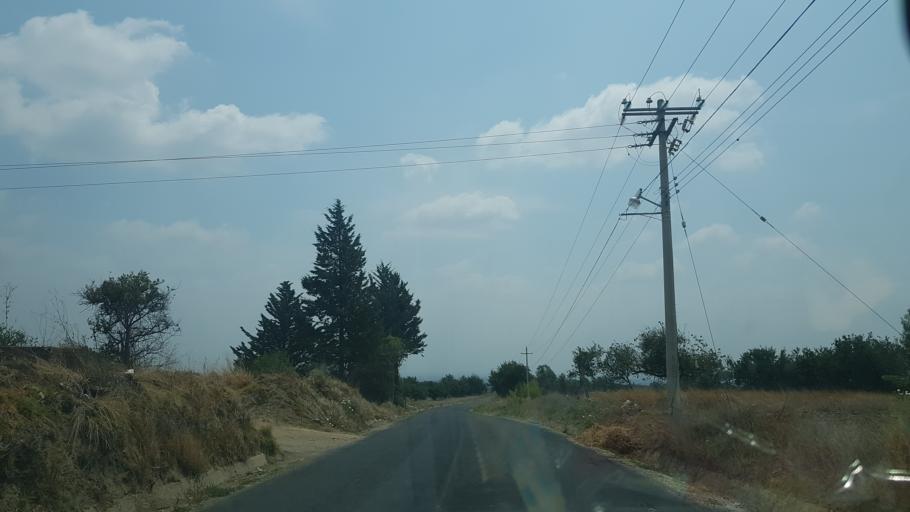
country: MX
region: Puebla
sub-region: Huejotzingo
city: San Juan Pancoac
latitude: 19.1378
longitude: -98.4256
